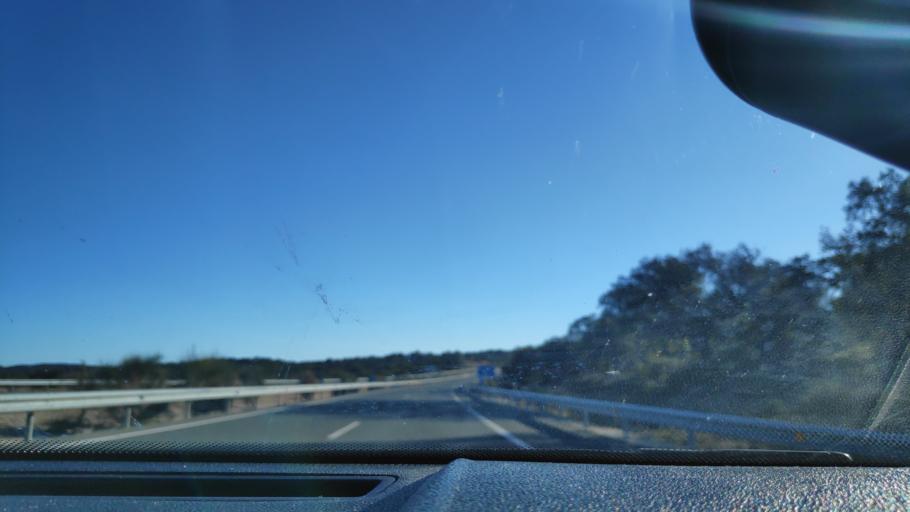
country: ES
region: Andalusia
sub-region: Provincia de Huelva
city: Santa Olalla del Cala
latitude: 37.9414
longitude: -6.2272
